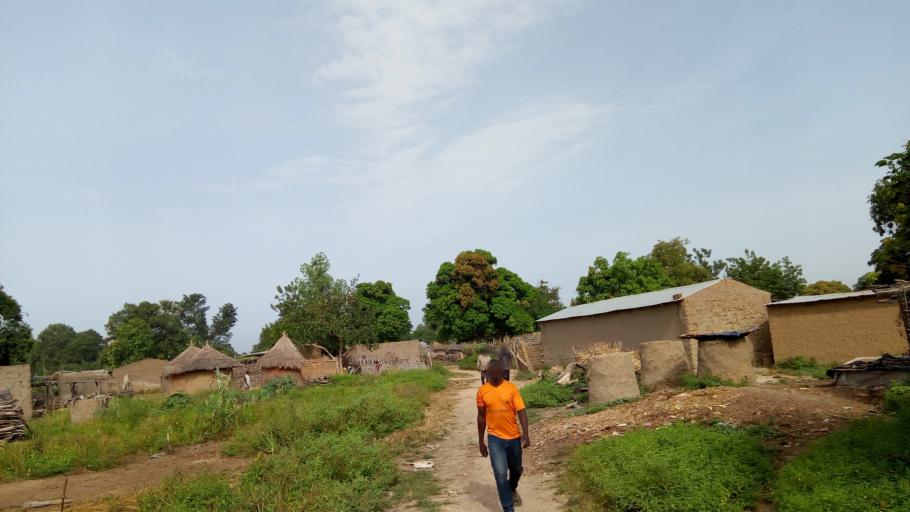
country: ML
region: Kayes
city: Kita
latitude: 13.1976
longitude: -8.7943
